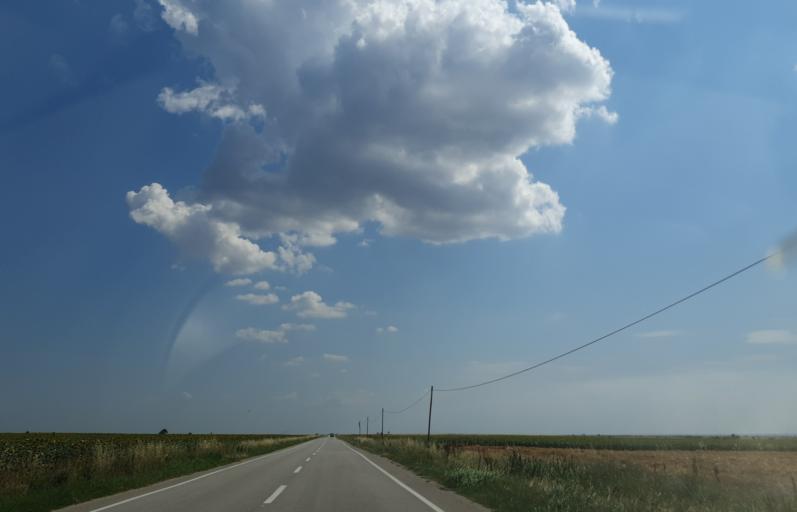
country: TR
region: Kirklareli
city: Buyukkaristiran
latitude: 41.4199
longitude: 27.5796
